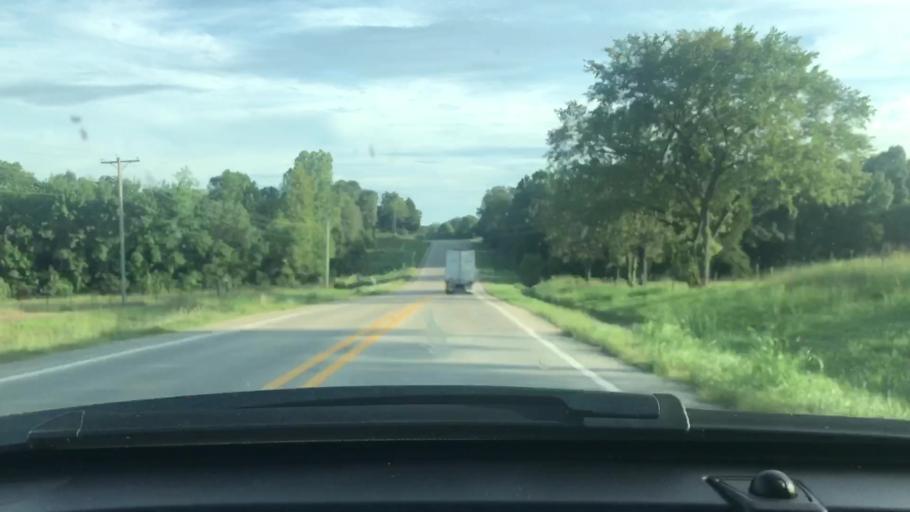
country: US
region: Arkansas
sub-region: Lawrence County
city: Hoxie
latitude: 36.1584
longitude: -91.1619
